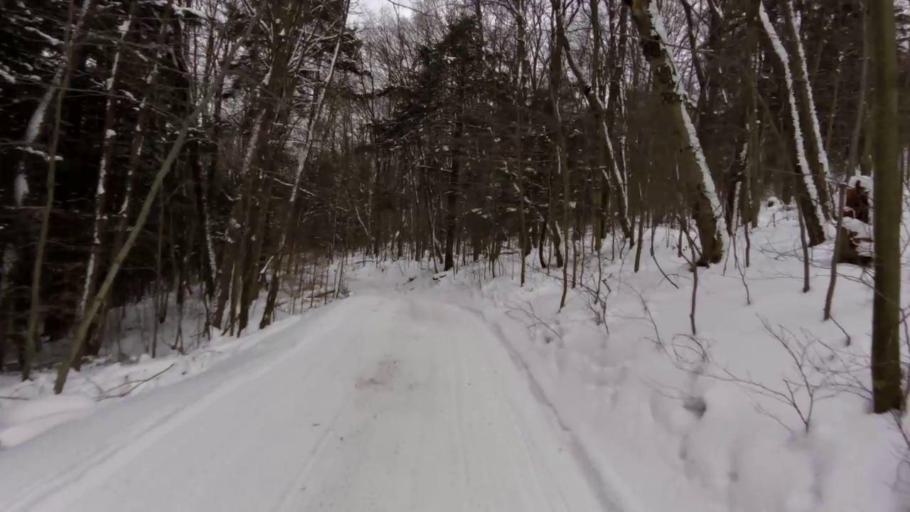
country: US
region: Pennsylvania
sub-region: McKean County
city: Bradford
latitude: 42.0168
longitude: -78.7238
